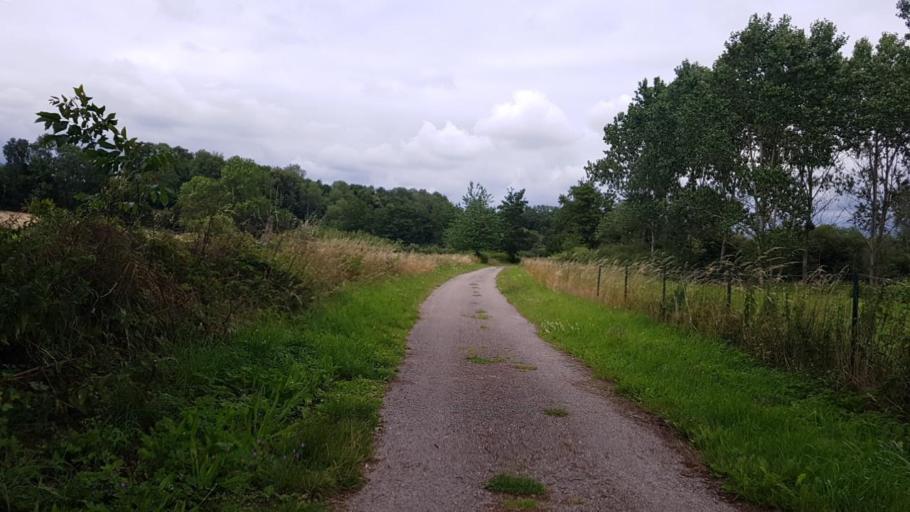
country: FR
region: Picardie
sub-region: Departement de l'Aisne
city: La Capelle
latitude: 49.9087
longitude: 3.9176
